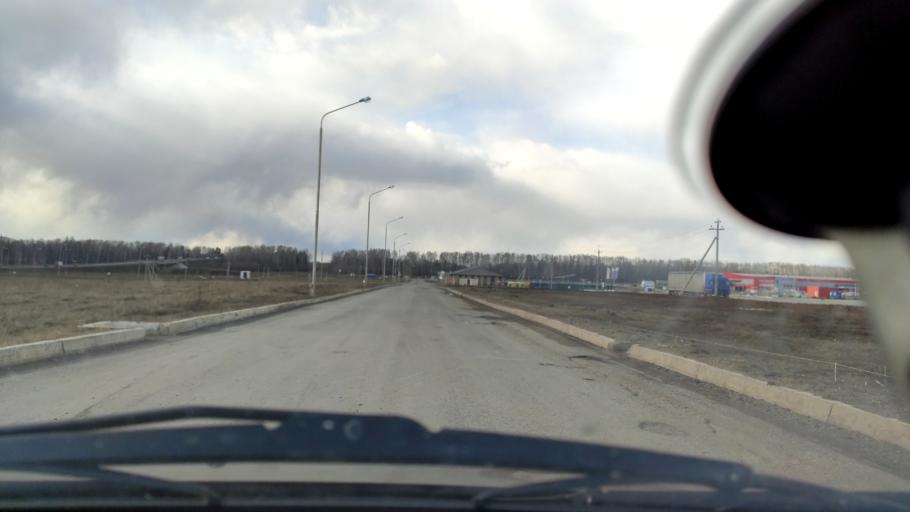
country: RU
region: Bashkortostan
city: Iglino
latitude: 54.7681
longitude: 56.2646
